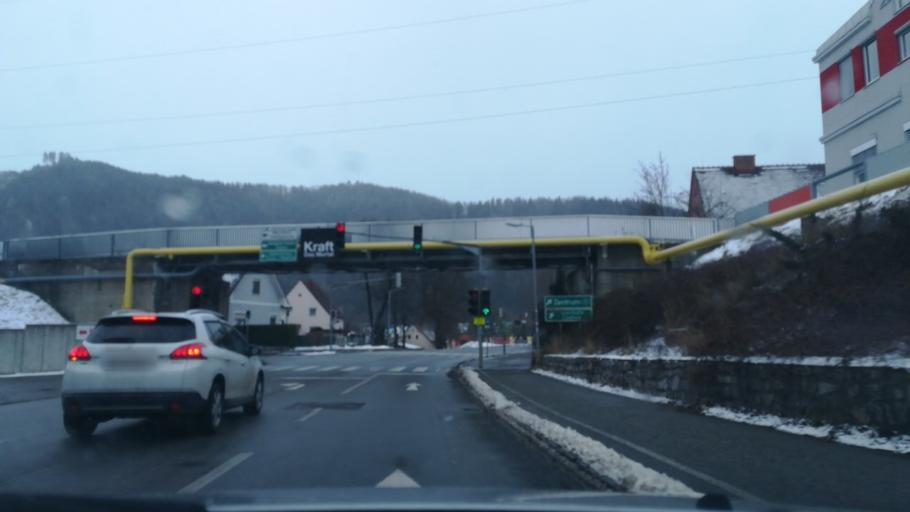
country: AT
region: Styria
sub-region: Politischer Bezirk Murtal
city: Judenburg
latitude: 47.1734
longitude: 14.6662
